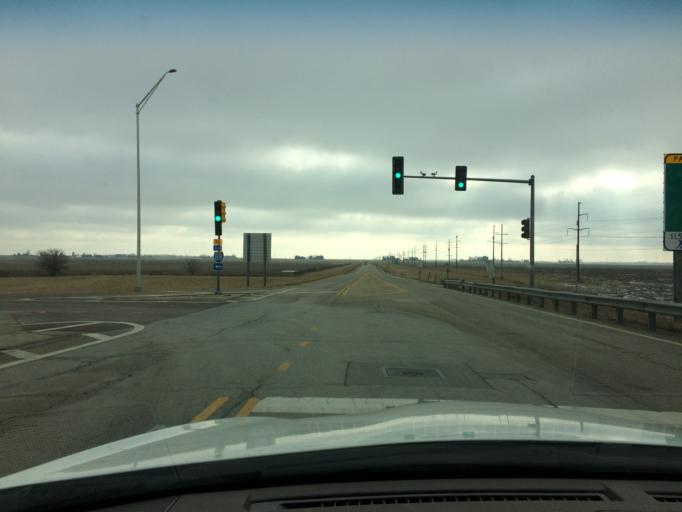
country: US
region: Illinois
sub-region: DeKalb County
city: DeKalb
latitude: 41.8989
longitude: -88.7240
